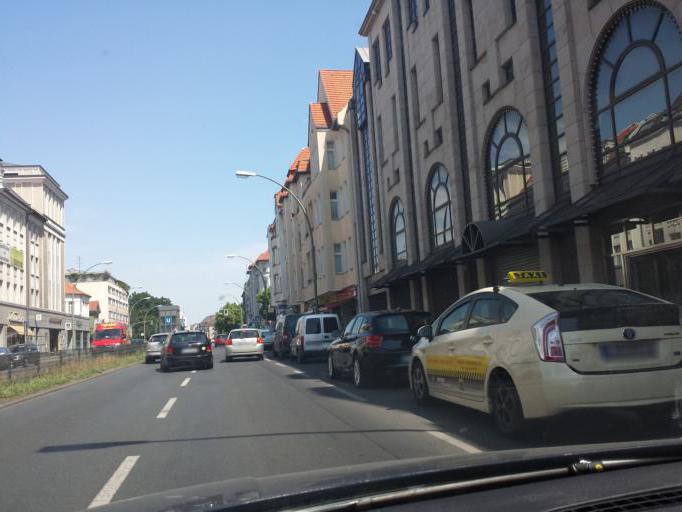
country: DE
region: Berlin
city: Tempelhof Bezirk
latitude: 52.4598
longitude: 13.3847
